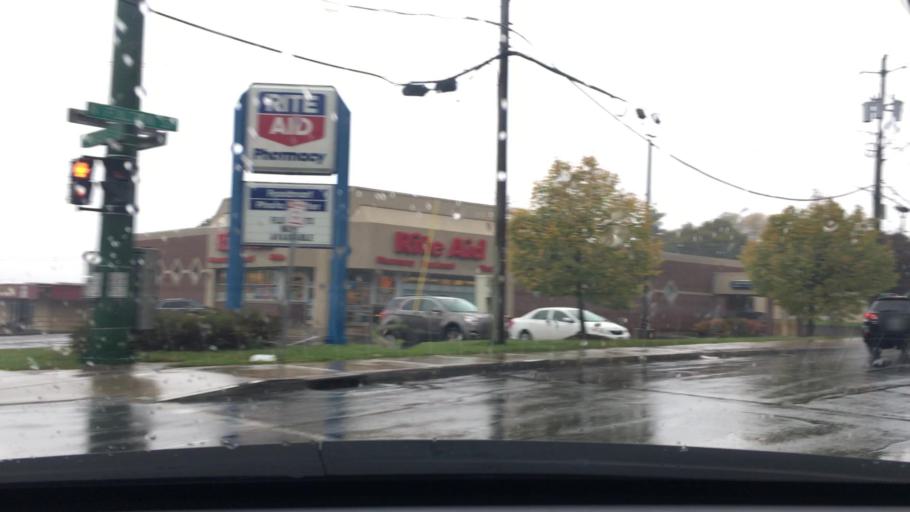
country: US
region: New York
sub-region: Cayuga County
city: Auburn
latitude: 42.9334
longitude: -76.5589
